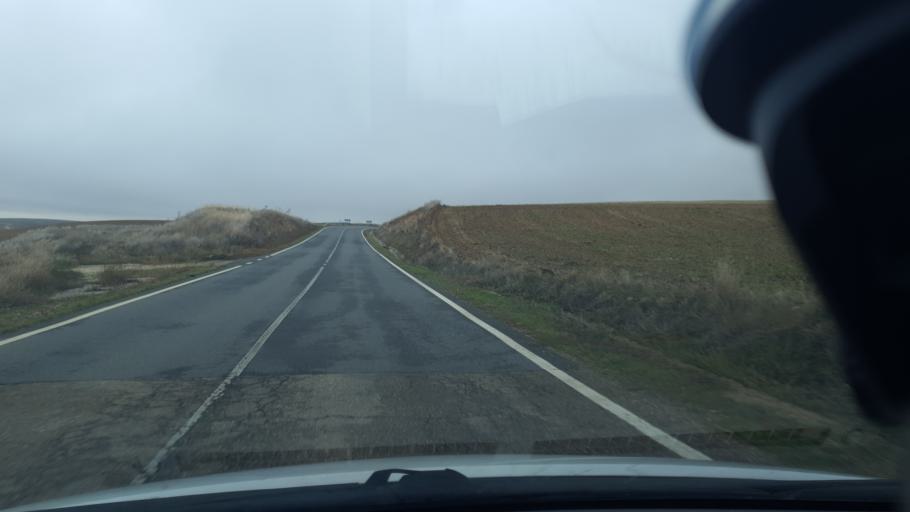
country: ES
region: Castille and Leon
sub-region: Provincia de Segovia
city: Valseca
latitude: 40.9952
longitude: -4.1837
